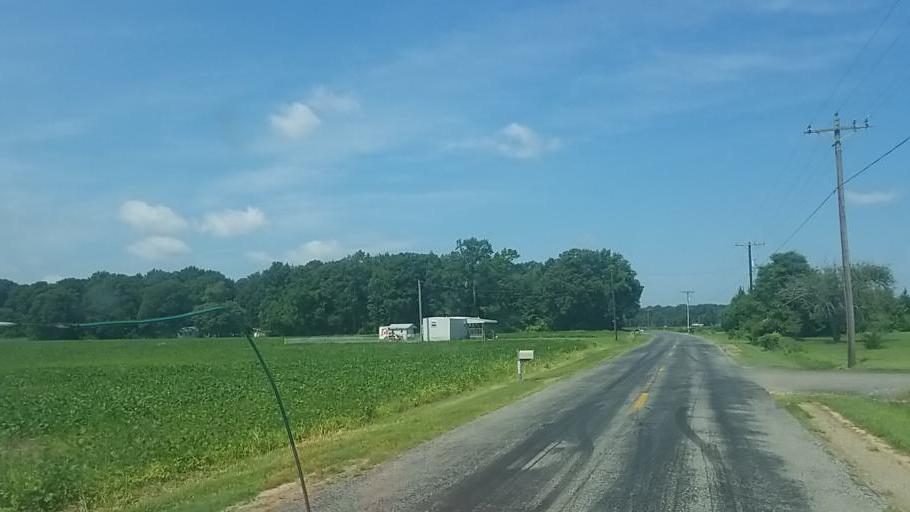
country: US
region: Maryland
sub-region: Caroline County
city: Denton
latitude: 38.8768
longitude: -75.7672
